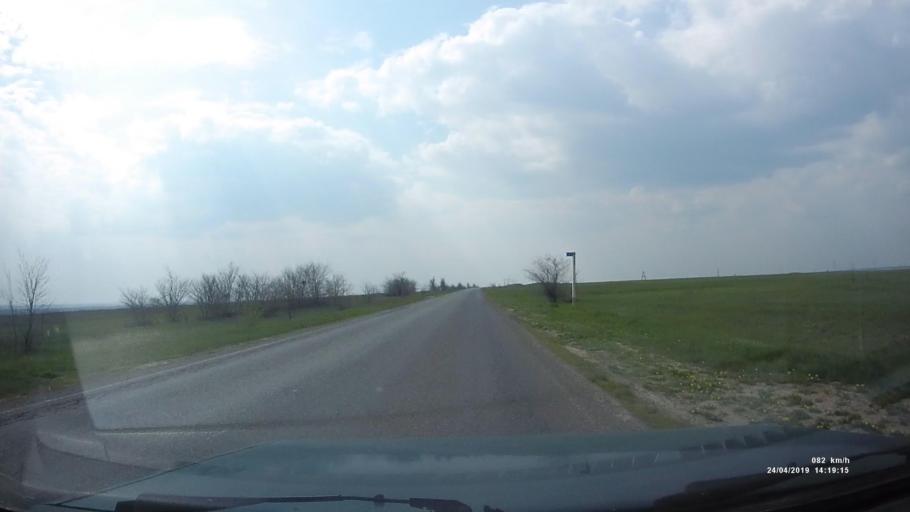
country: RU
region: Kalmykiya
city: Arshan'
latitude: 46.3049
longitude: 44.1790
